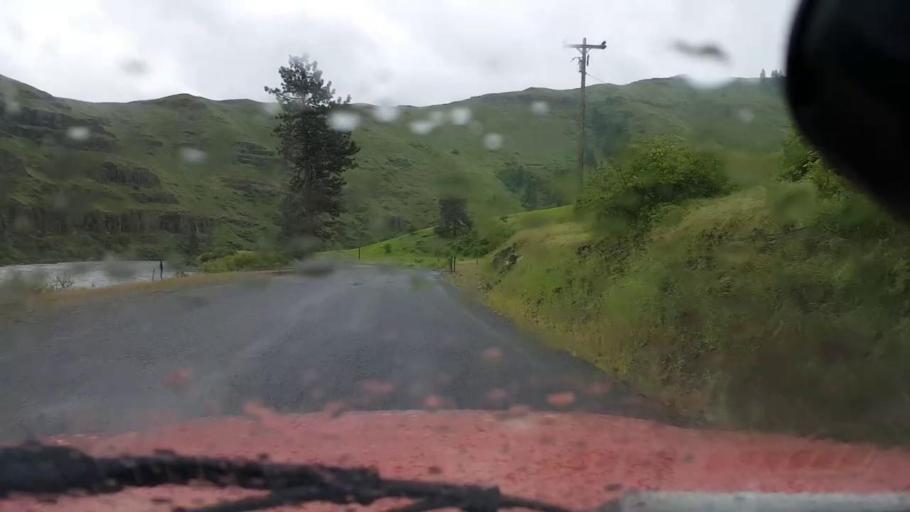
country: US
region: Washington
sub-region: Asotin County
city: Asotin
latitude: 46.0306
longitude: -117.3278
